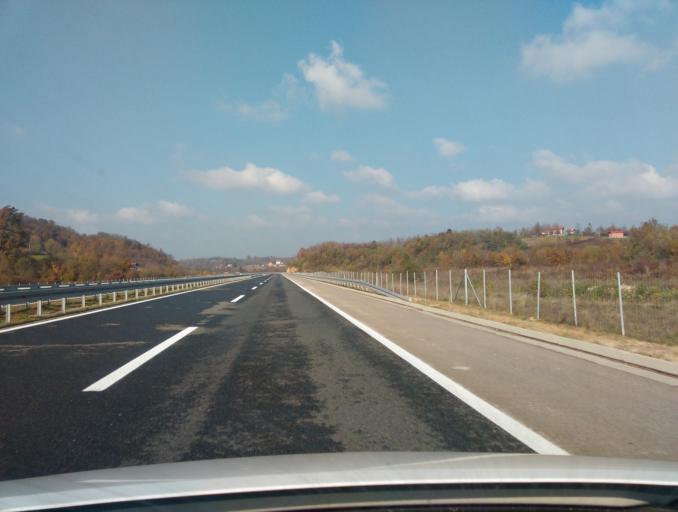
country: BA
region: Republika Srpska
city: Doboj
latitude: 44.8261
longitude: 18.0203
